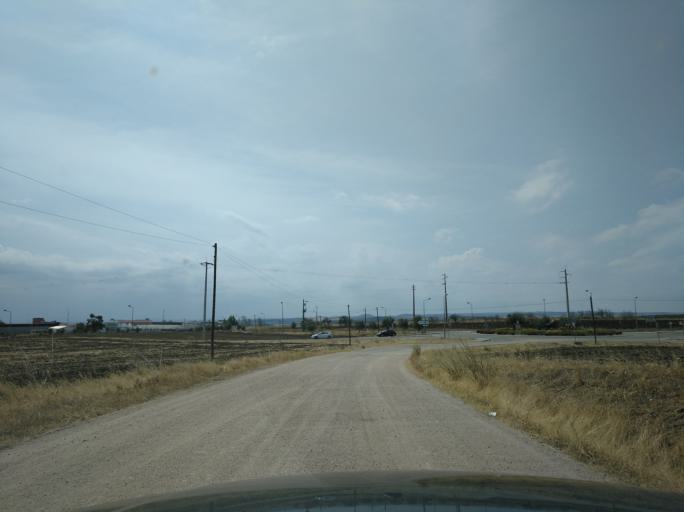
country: PT
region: Portalegre
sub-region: Campo Maior
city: Campo Maior
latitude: 39.0268
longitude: -7.0671
